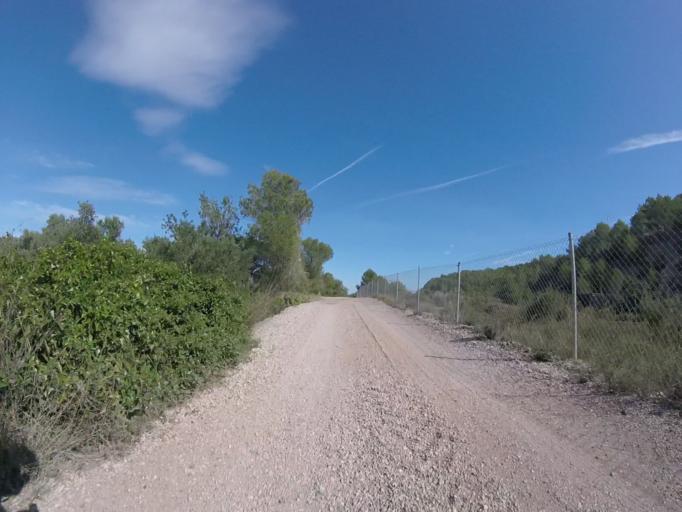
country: ES
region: Valencia
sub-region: Provincia de Castello
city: Santa Magdalena de Pulpis
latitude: 40.3872
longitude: 0.3462
